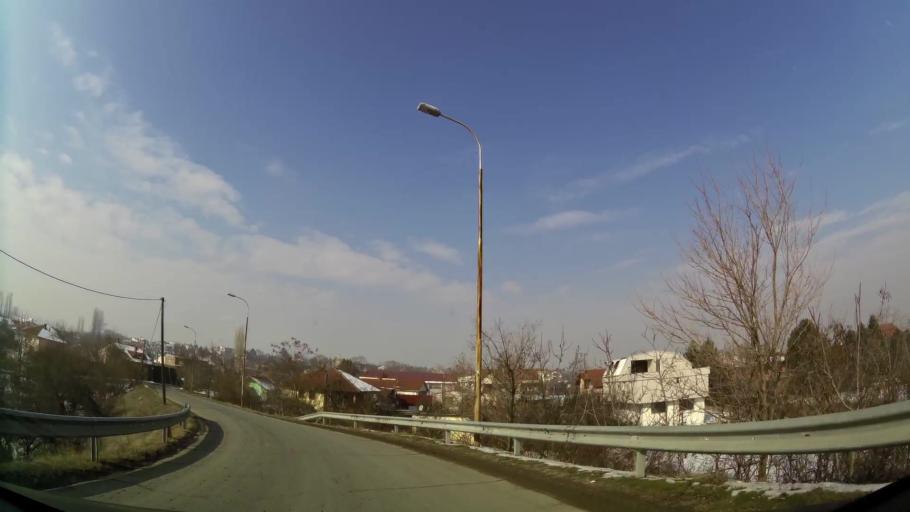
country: MK
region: Suto Orizari
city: Suto Orizare
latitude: 42.0249
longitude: 21.3843
